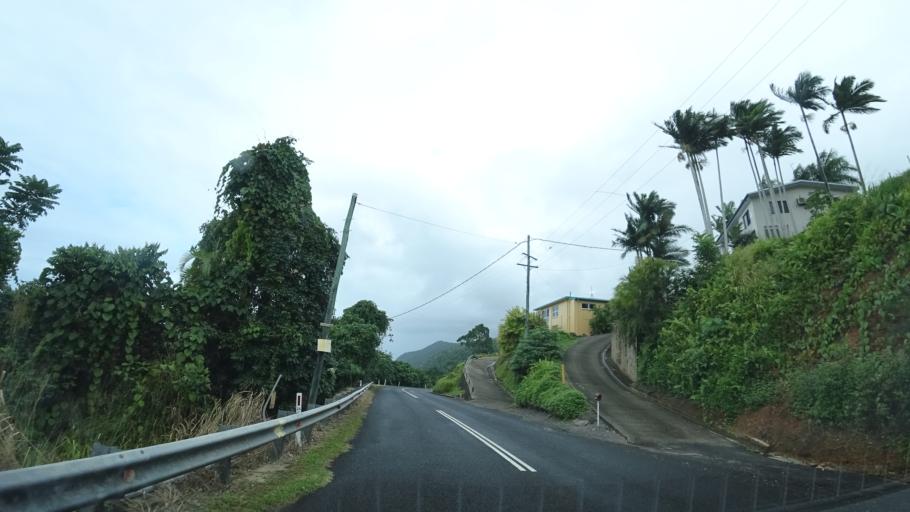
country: AU
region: Queensland
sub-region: Cassowary Coast
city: Innisfail
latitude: -17.5568
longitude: 146.0880
